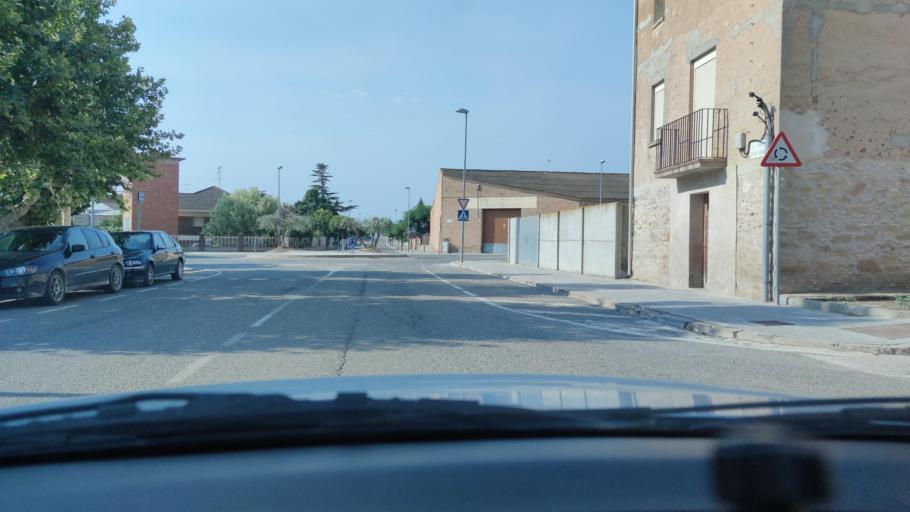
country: ES
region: Catalonia
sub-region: Provincia de Lleida
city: Juneda
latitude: 41.5791
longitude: 0.8322
